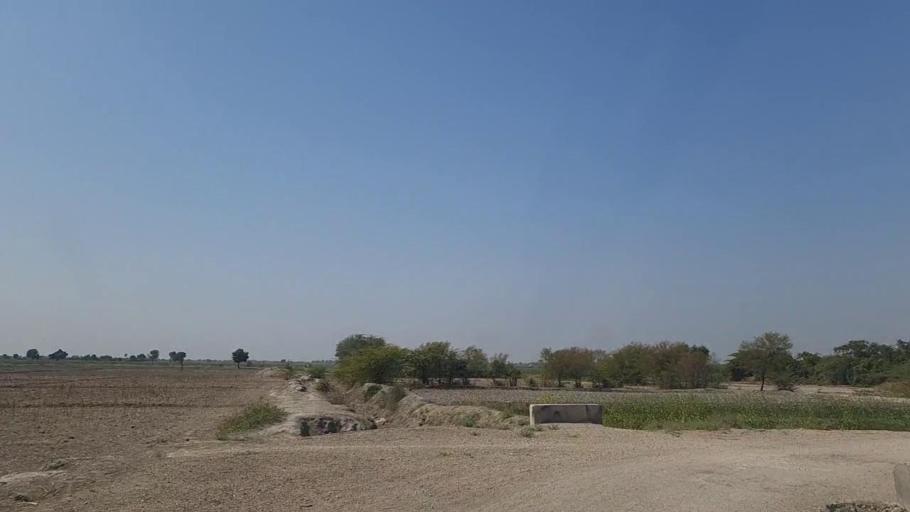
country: PK
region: Sindh
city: Naukot
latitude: 24.8732
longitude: 69.4268
